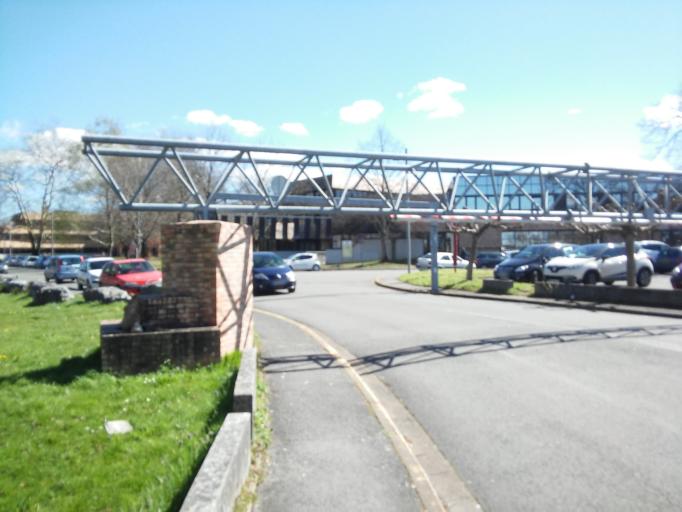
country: FR
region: Aquitaine
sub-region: Departement des Pyrenees-Atlantiques
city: Pau
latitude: 43.3169
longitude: -0.3679
